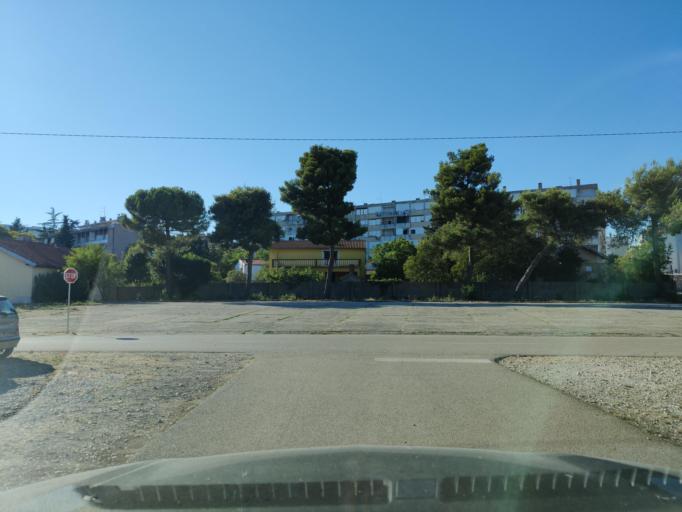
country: HR
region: Zadarska
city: Zadar
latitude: 44.1147
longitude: 15.2381
